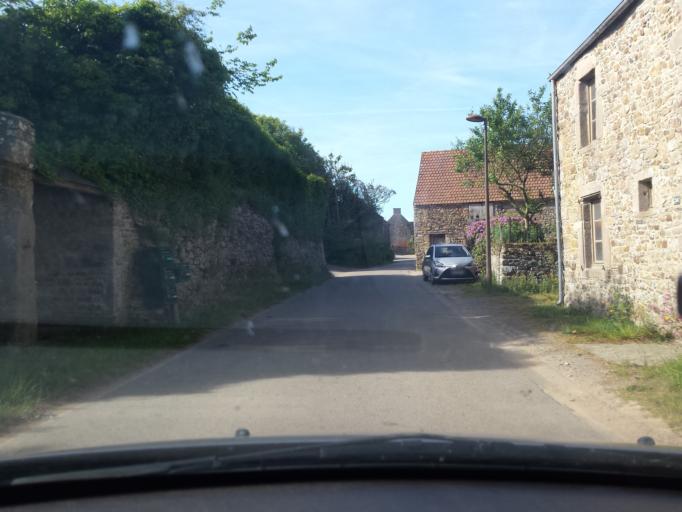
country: FR
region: Lower Normandy
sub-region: Departement de la Manche
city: Beaumont-Hague
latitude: 49.6797
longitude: -1.9212
